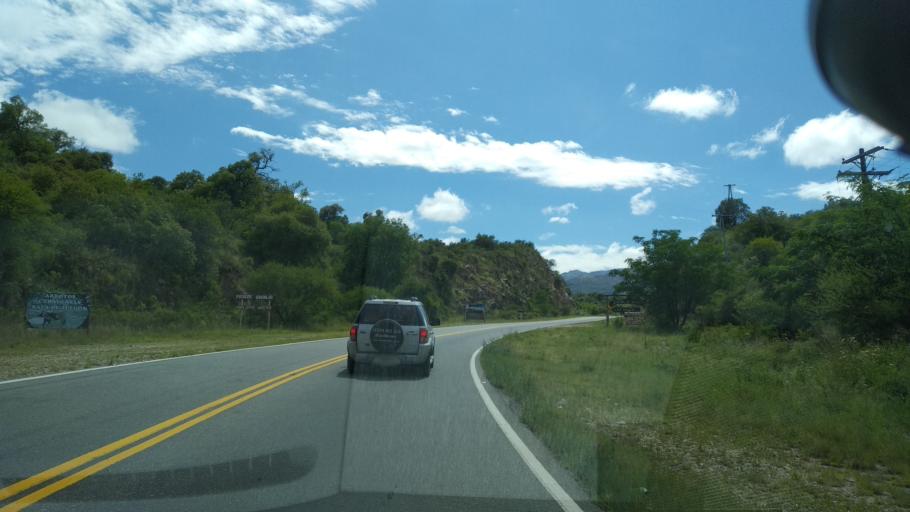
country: AR
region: Cordoba
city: Mina Clavero
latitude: -31.7605
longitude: -64.9619
